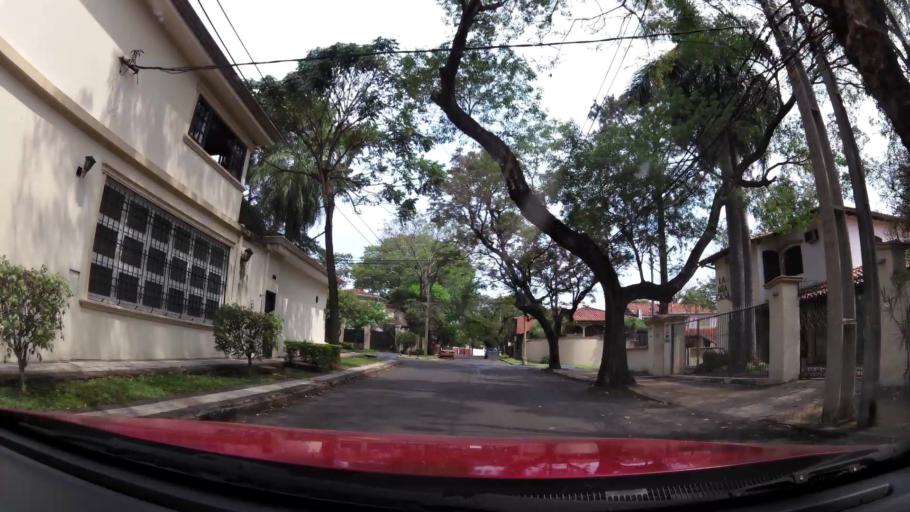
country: PY
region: Asuncion
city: Asuncion
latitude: -25.2869
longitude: -57.5838
